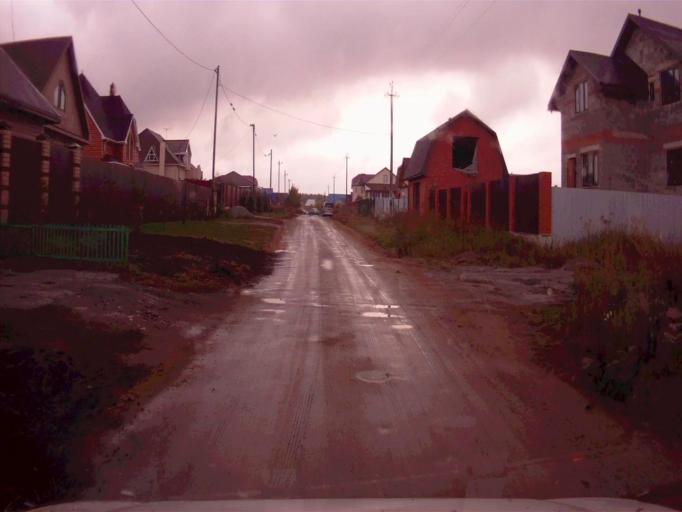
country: RU
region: Chelyabinsk
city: Dolgoderevenskoye
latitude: 55.3082
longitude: 61.3413
